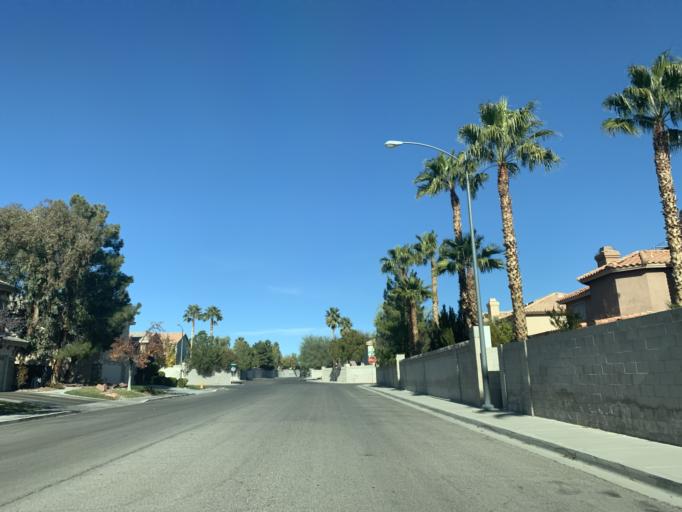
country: US
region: Nevada
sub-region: Clark County
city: Summerlin South
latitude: 36.1216
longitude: -115.2925
